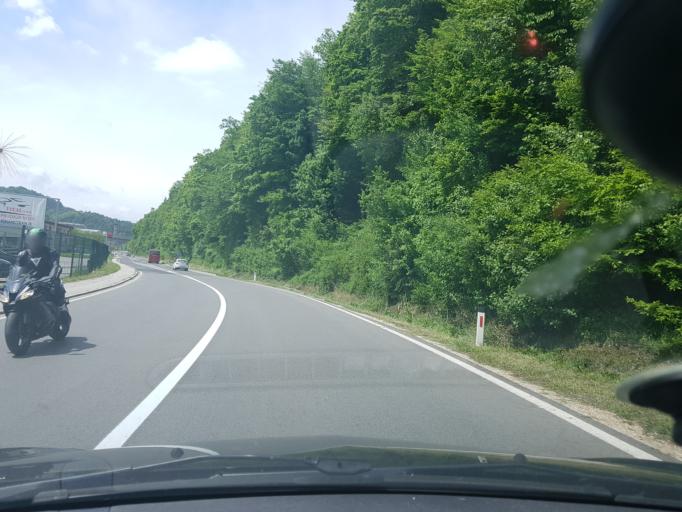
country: SI
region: Store
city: Store
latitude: 46.2238
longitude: 15.3158
